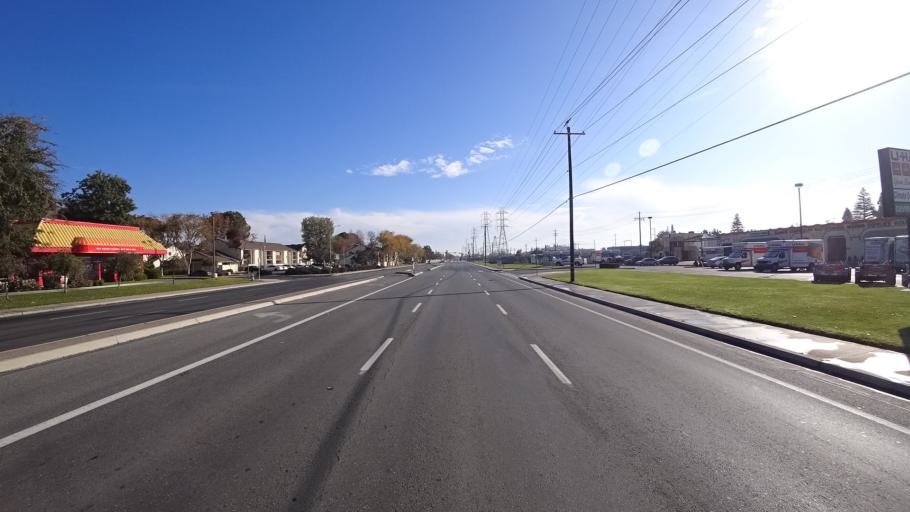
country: US
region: California
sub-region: Kern County
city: Greenacres
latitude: 35.3181
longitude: -119.0718
